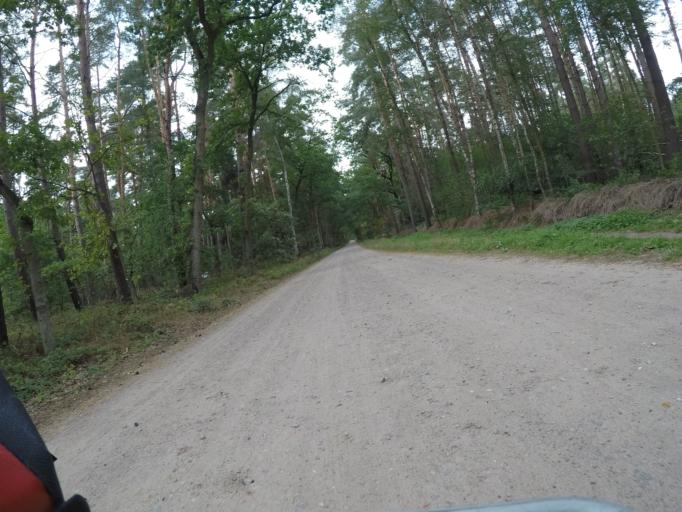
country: DE
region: Lower Saxony
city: Wittorf
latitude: 53.3205
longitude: 10.3986
